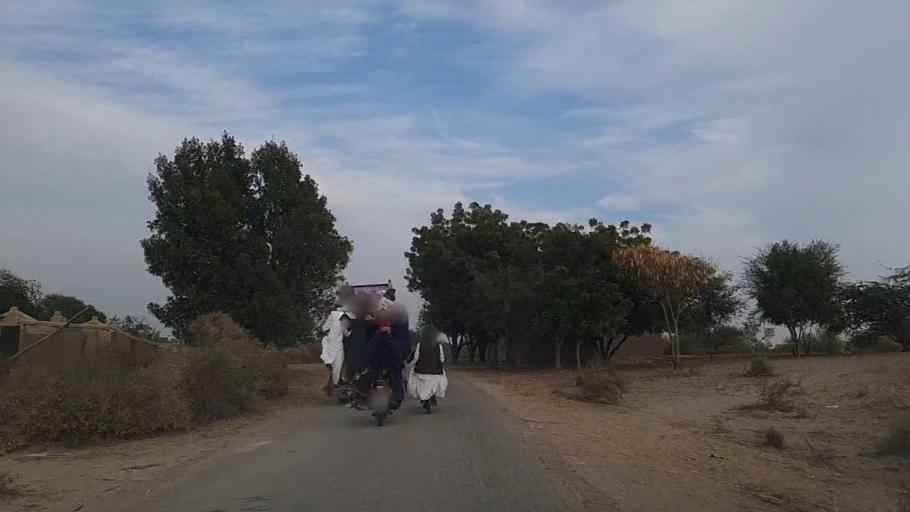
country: PK
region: Sindh
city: Daur
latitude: 26.5270
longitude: 68.4144
